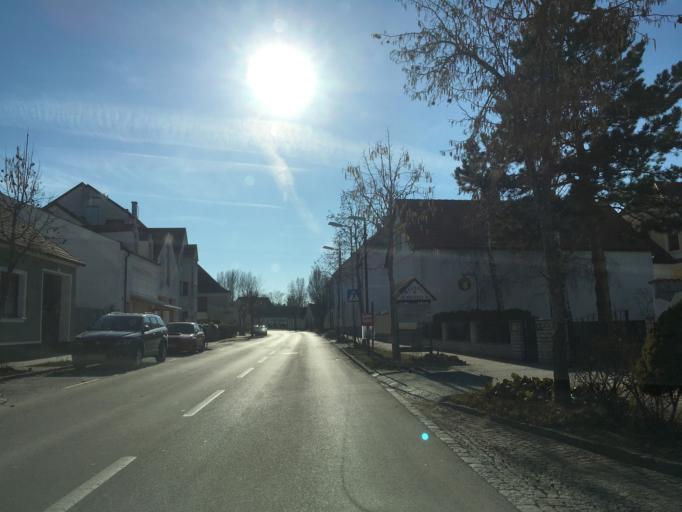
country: AT
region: Burgenland
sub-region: Eisenstadt-Umgebung
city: Wimpassing an der Leitha
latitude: 47.9179
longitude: 16.4292
